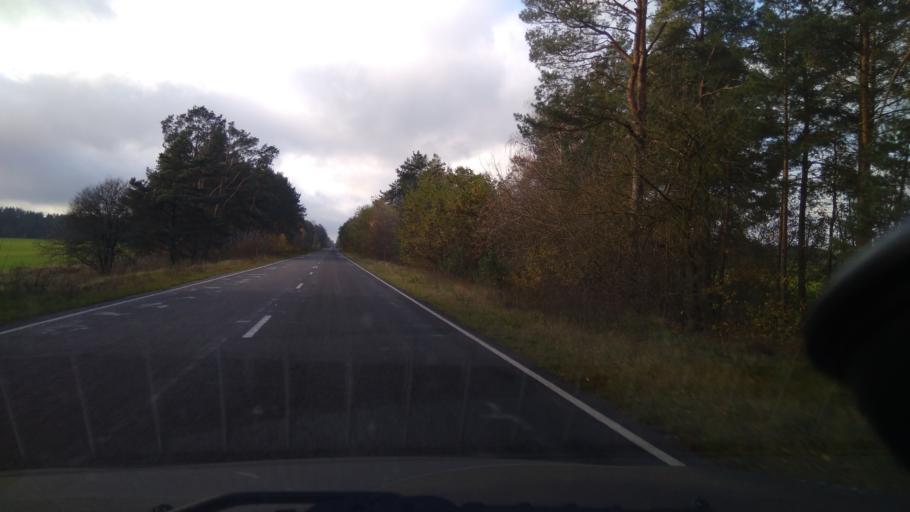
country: BY
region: Minsk
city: Urechcha
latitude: 53.2099
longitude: 27.9871
